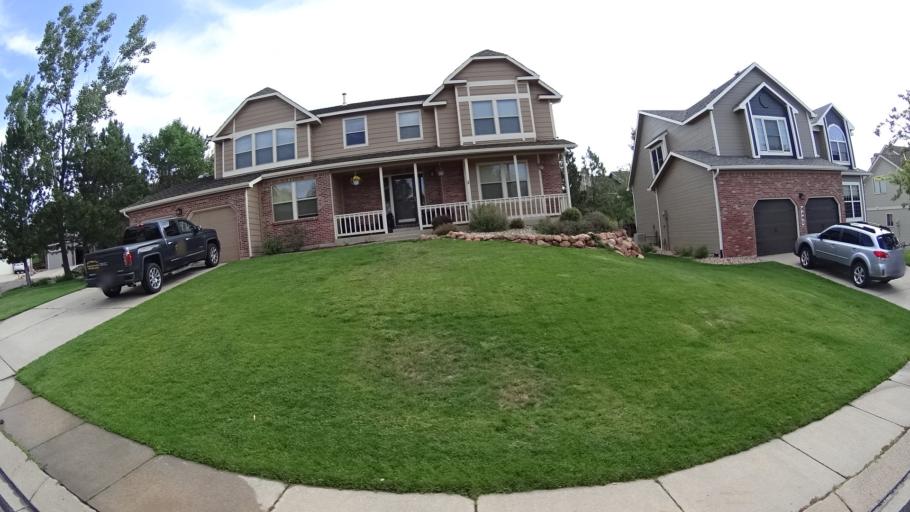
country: US
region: Colorado
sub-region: El Paso County
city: Air Force Academy
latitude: 38.9520
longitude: -104.8622
